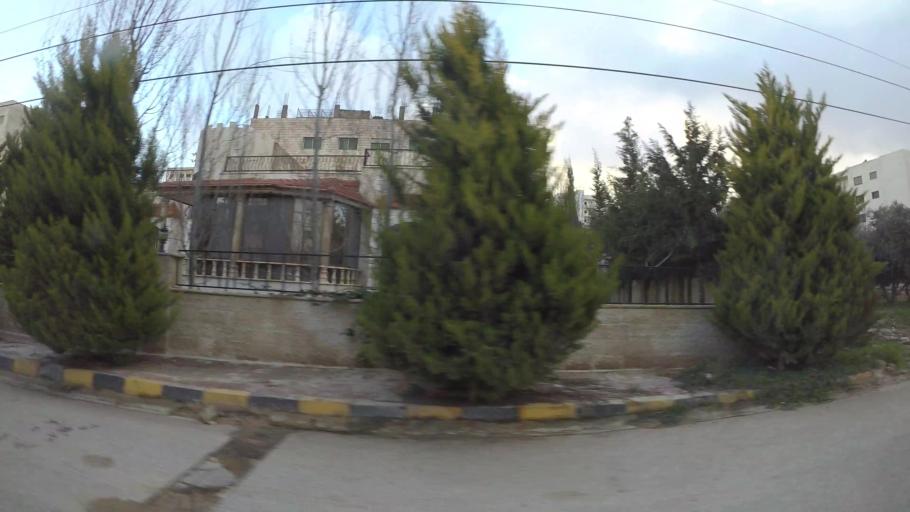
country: JO
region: Amman
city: Al Jubayhah
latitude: 32.0520
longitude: 35.8967
